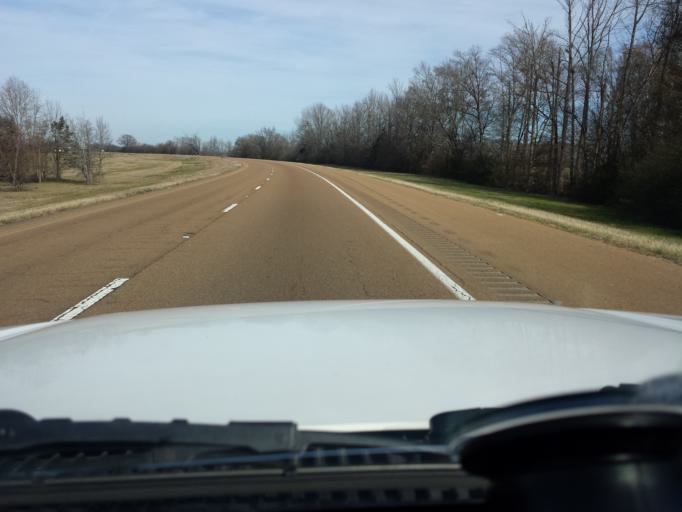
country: US
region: Mississippi
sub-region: Madison County
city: Canton
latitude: 32.6214
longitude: -90.0638
